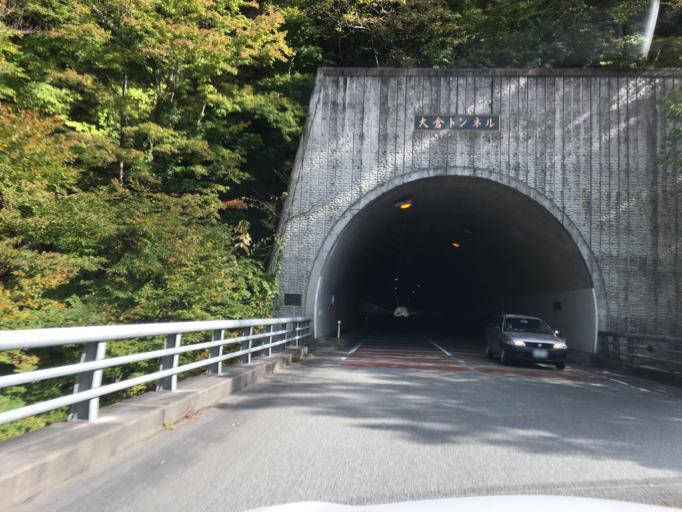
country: JP
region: Fukushima
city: Namie
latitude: 37.3592
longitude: 140.9297
